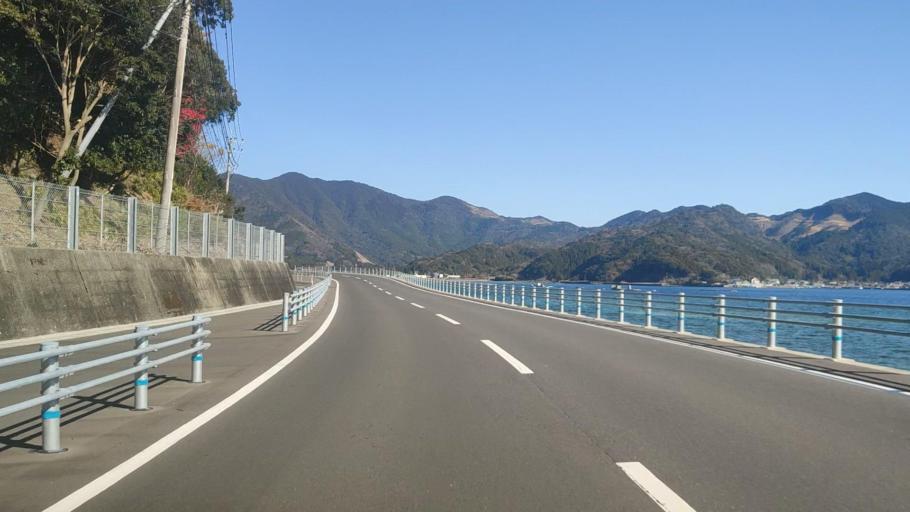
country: JP
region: Oita
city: Saiki
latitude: 32.7944
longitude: 131.8867
